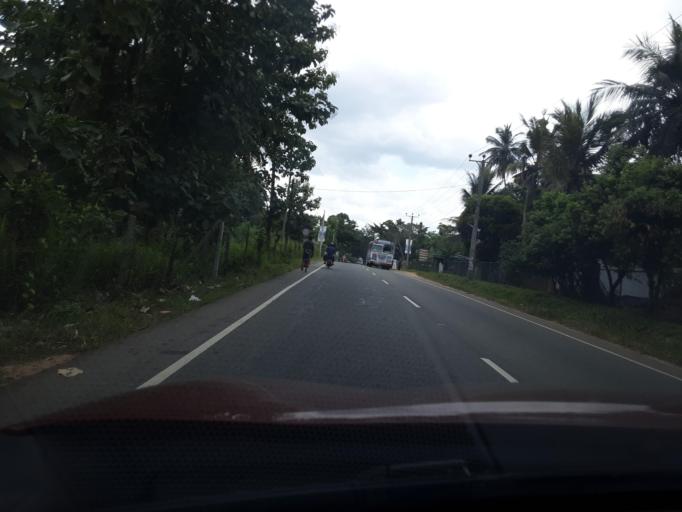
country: LK
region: North Western
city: Kurunegala
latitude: 7.4423
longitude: 80.2055
